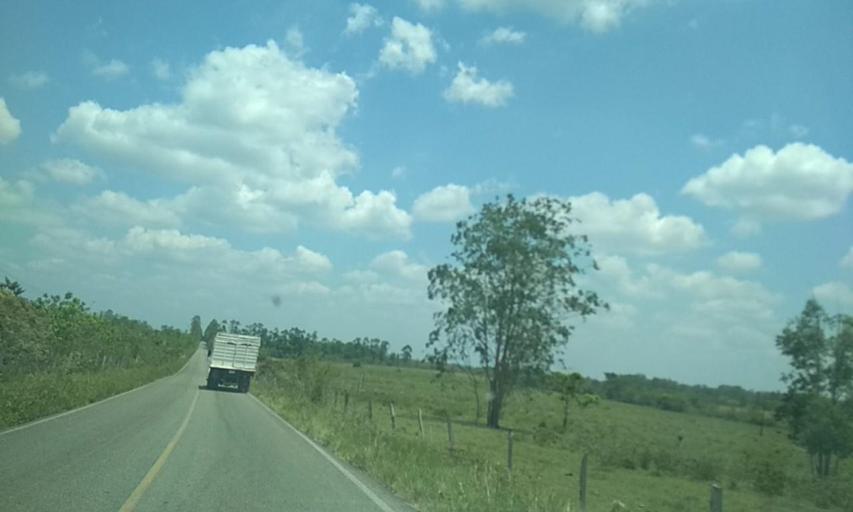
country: MX
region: Tabasco
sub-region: Huimanguillo
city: Francisco Rueda
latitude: 17.7676
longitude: -93.7999
